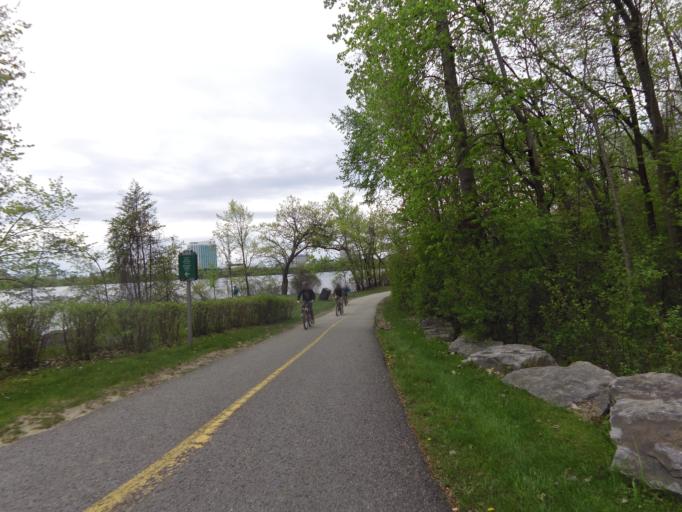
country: CA
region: Quebec
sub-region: Outaouais
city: Gatineau
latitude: 45.4544
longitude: -75.7214
